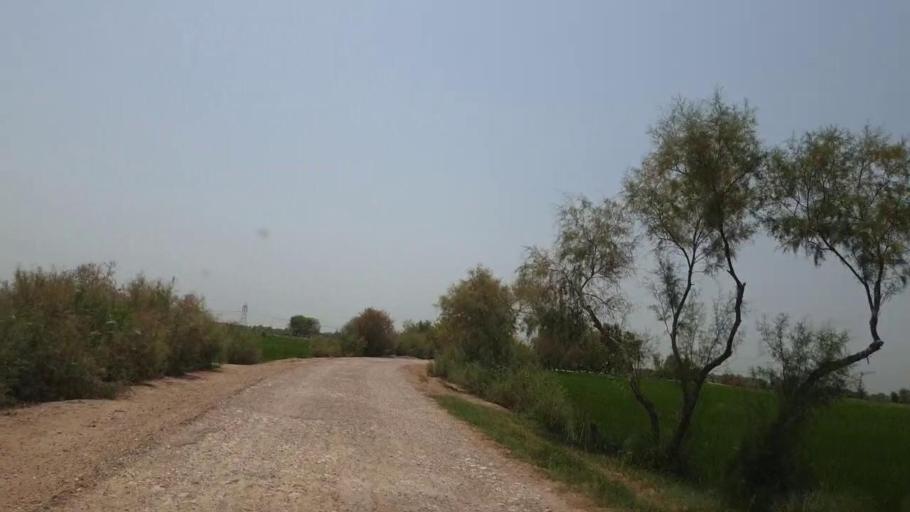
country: PK
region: Sindh
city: Shikarpur
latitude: 27.8985
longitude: 68.6320
